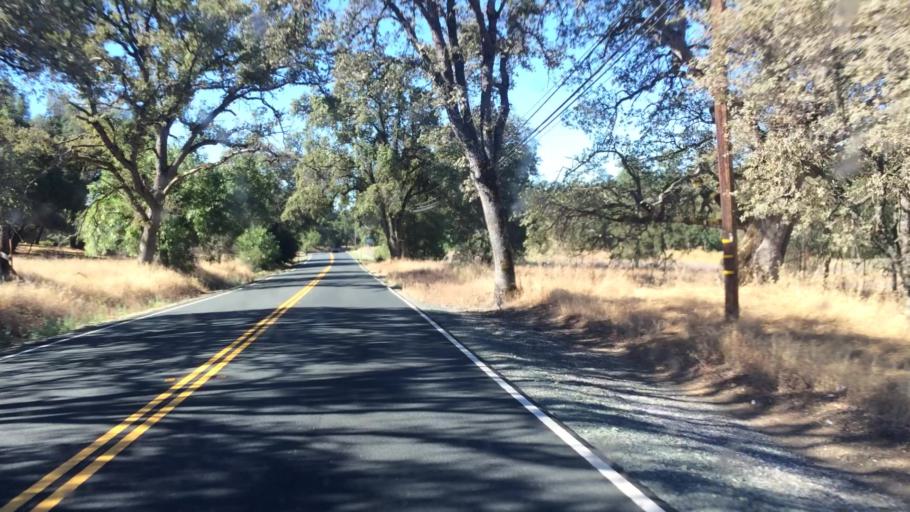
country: US
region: California
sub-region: El Dorado County
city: Deer Park
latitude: 38.6703
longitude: -120.8524
